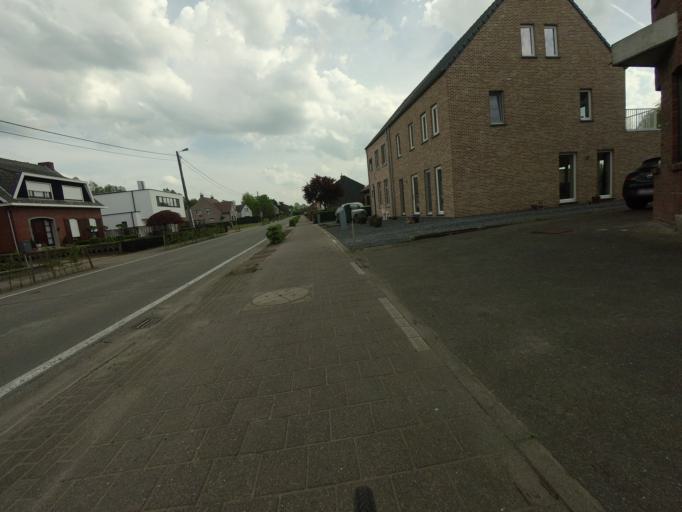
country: BE
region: Flanders
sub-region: Provincie Antwerpen
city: Putte
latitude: 51.0609
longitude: 4.6355
